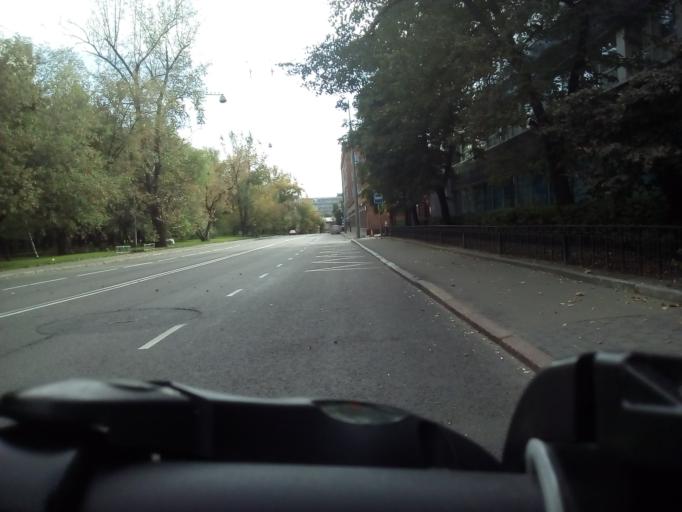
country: RU
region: Moskovskaya
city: Bogorodskoye
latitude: 55.7916
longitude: 37.7077
